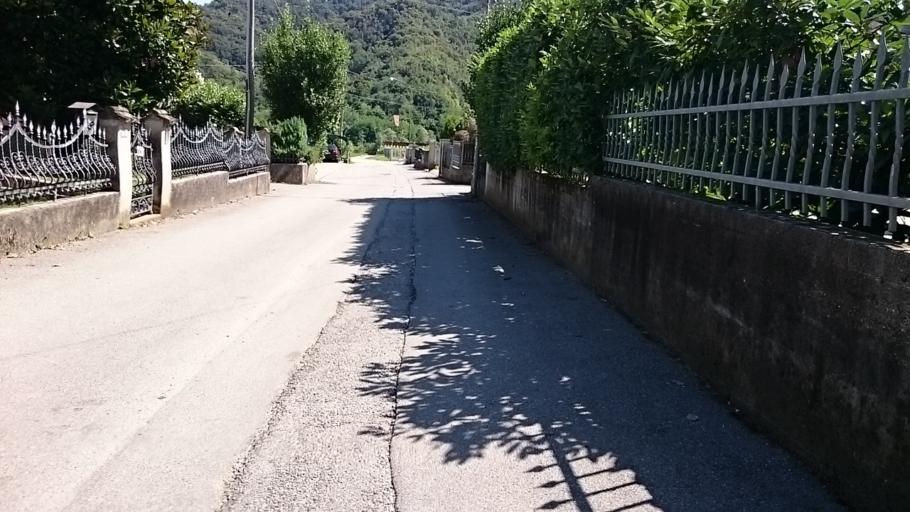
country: IT
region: Veneto
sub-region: Provincia di Treviso
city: Miane
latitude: 45.9293
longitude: 12.1063
